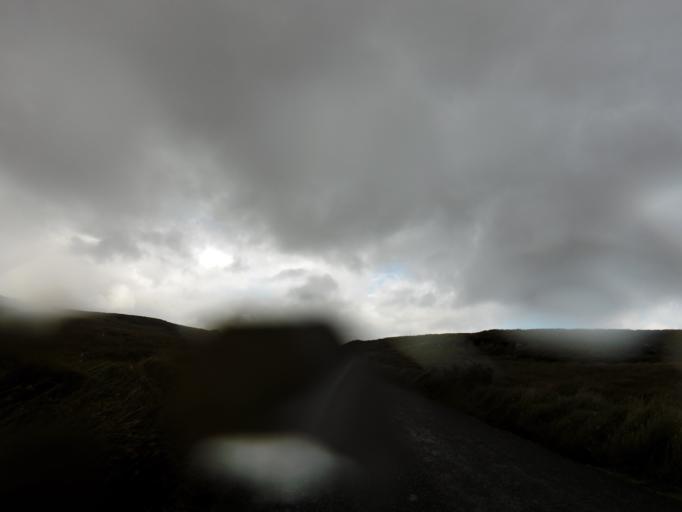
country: IE
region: Connaught
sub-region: County Galway
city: Oughterard
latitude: 53.3941
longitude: -9.3378
